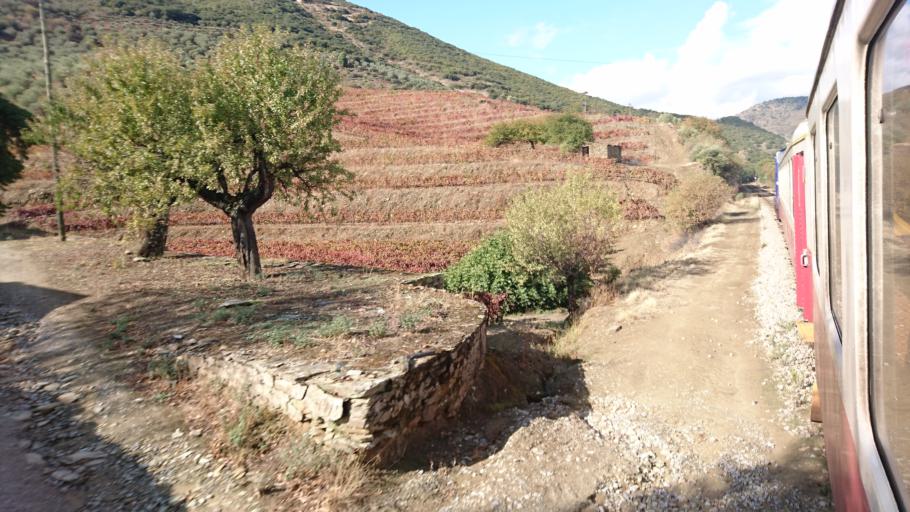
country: PT
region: Guarda
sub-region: Vila Nova de Foz Coa
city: Vila Nova de Foz Coa
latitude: 41.1388
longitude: -7.2359
